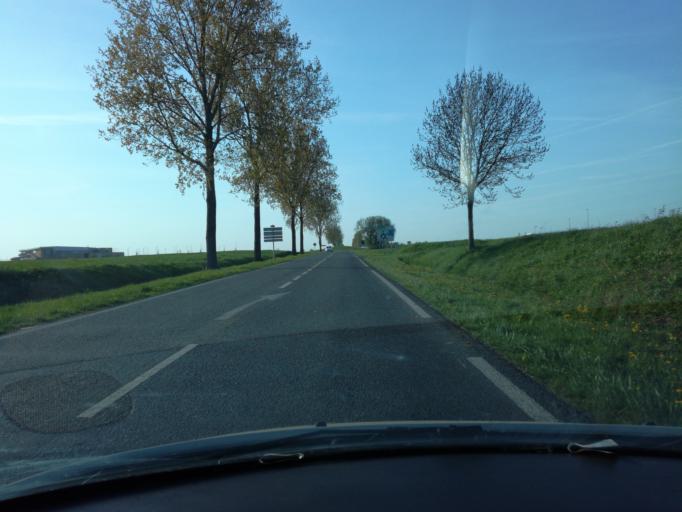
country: FR
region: Picardie
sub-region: Departement de la Somme
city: Poix-de-Picardie
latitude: 49.8050
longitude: 1.9688
